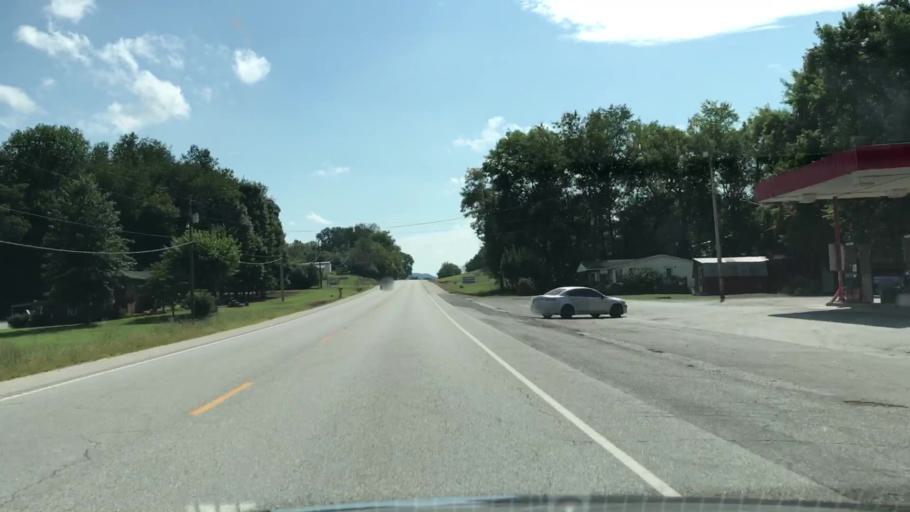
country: US
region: Tennessee
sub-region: Trousdale County
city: Hartsville
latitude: 36.3596
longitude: -86.0513
